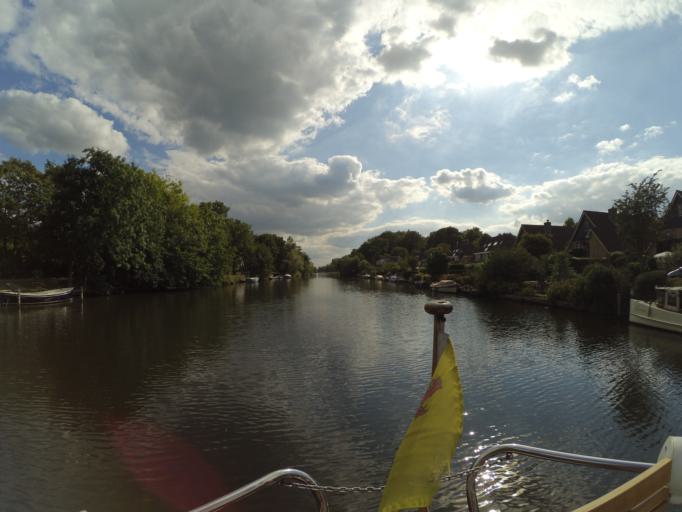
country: NL
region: Utrecht
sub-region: Stichtse Vecht
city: Breukelen
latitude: 52.1676
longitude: 5.0094
